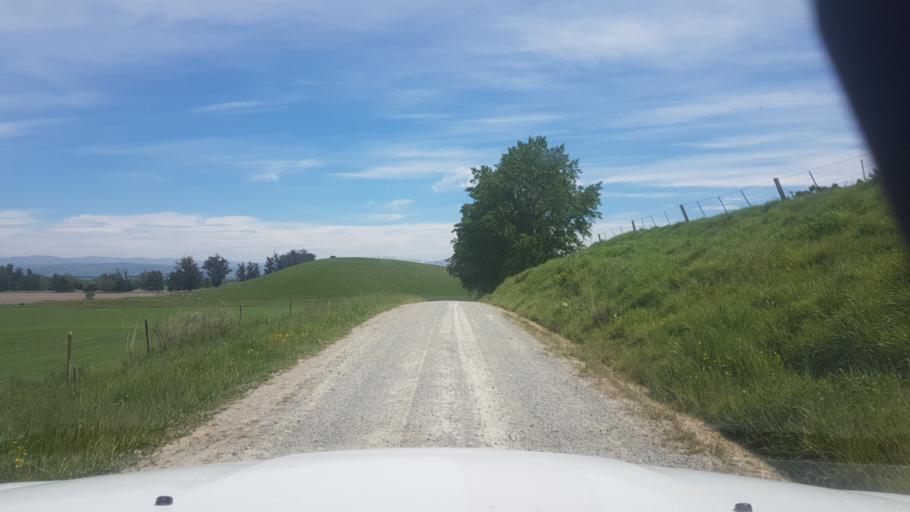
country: NZ
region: Canterbury
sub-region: Timaru District
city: Pleasant Point
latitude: -44.1967
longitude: 171.1088
